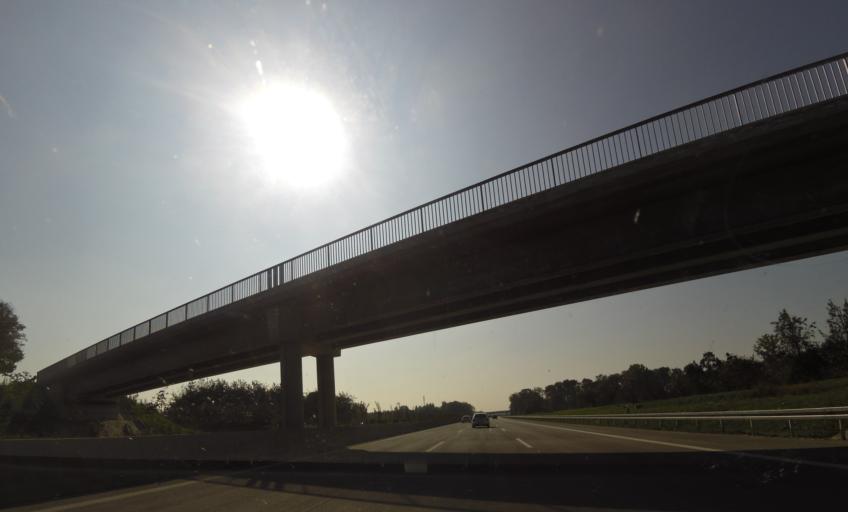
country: DE
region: Baden-Wuerttemberg
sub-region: Karlsruhe Region
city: Zell
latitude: 48.6819
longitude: 8.0615
